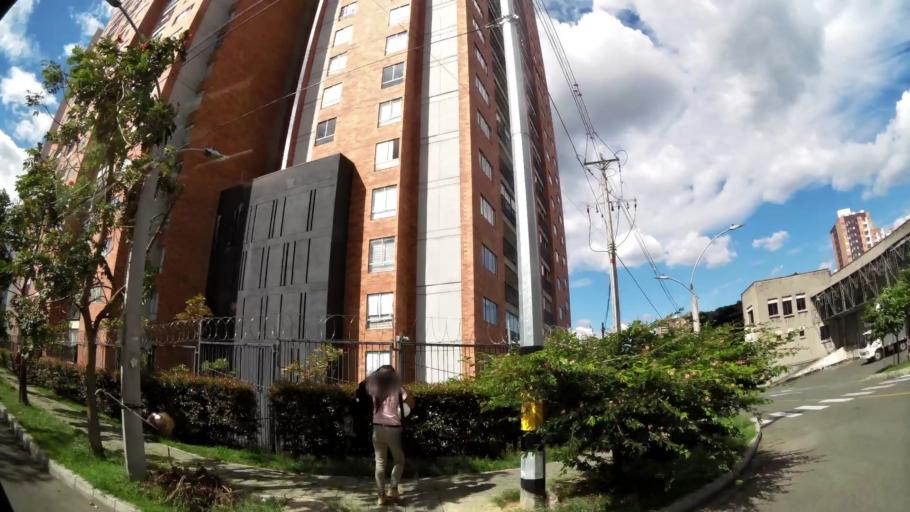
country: CO
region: Antioquia
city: Sabaneta
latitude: 6.1564
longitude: -75.6091
